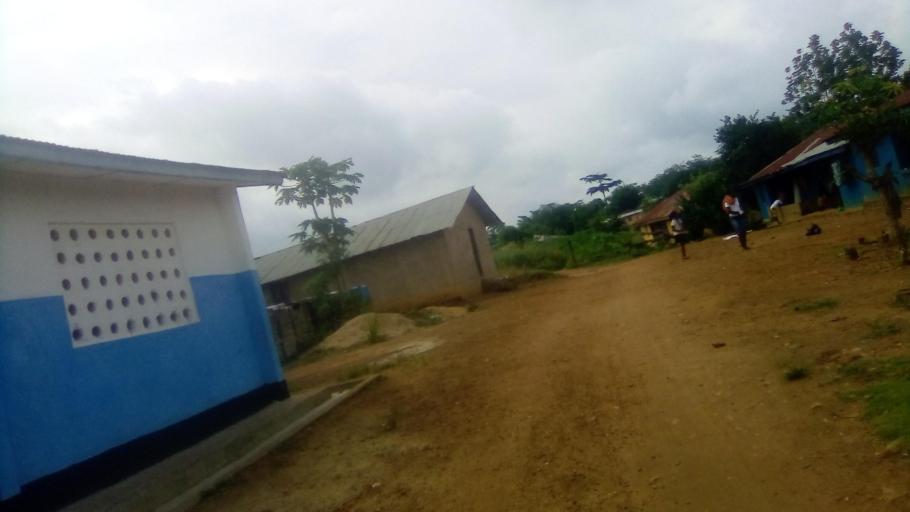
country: SL
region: Eastern Province
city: Kailahun
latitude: 8.2712
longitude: -10.5639
